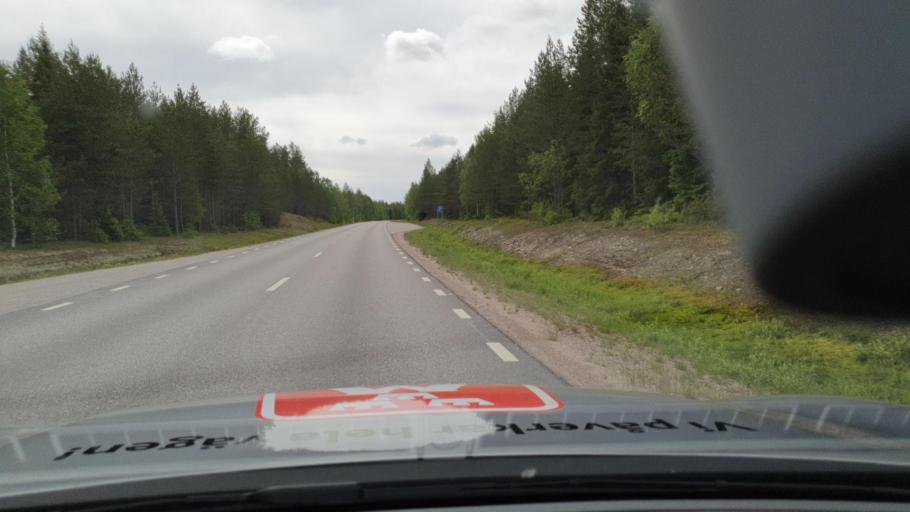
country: SE
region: Norrbotten
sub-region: Kalix Kommun
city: Kalix
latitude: 65.8667
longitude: 23.4855
